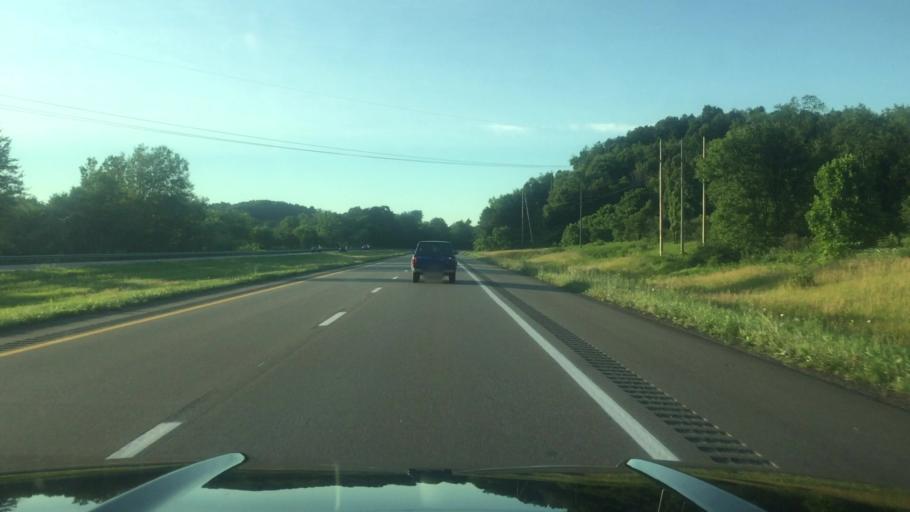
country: US
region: Ohio
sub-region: Tuscarawas County
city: Newcomerstown
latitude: 40.3344
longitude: -81.5699
